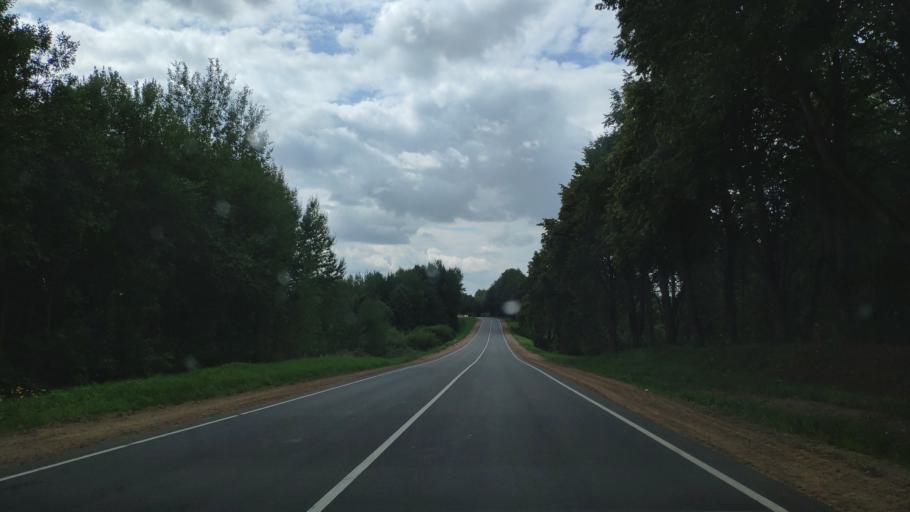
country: BY
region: Minsk
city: Syomkava
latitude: 54.0083
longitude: 27.3862
